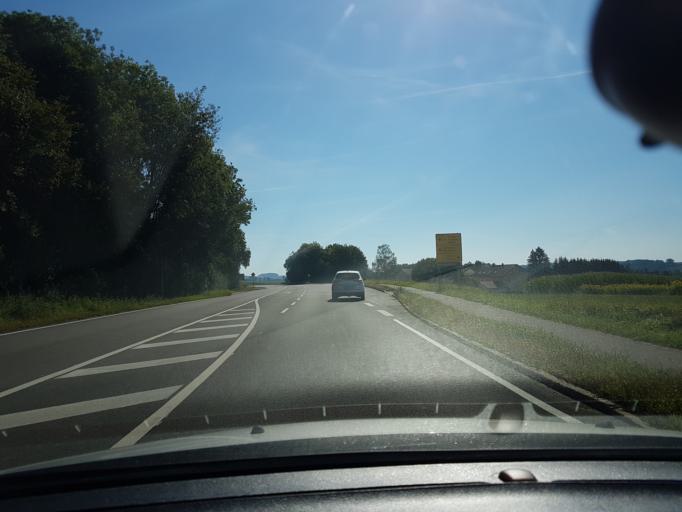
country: DE
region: Bavaria
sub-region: Upper Bavaria
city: Aham
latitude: 48.3509
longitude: 12.1791
